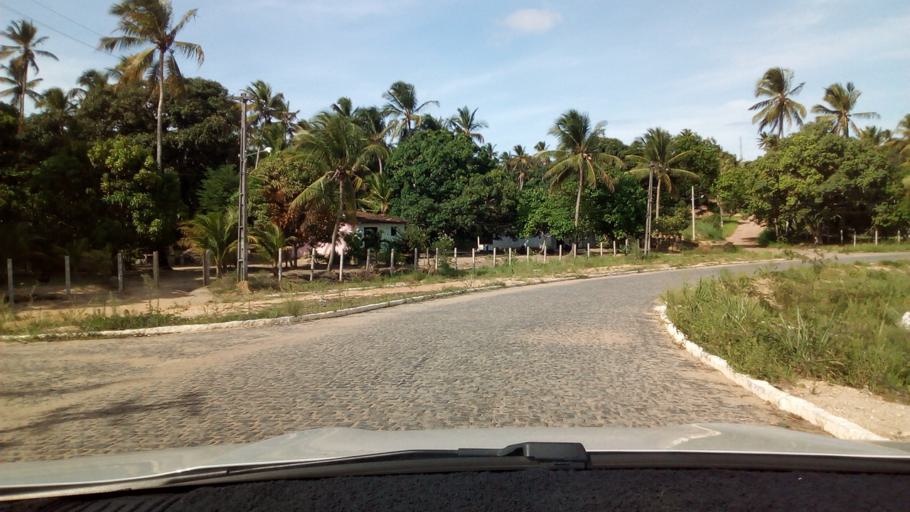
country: BR
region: Paraiba
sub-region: Joao Pessoa
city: Joao Pessoa
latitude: -7.0514
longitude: -34.9047
